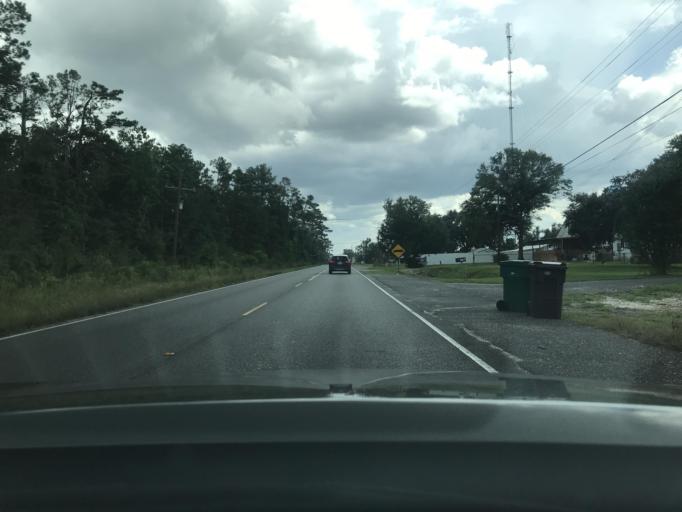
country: US
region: Louisiana
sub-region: Calcasieu Parish
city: Westlake
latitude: 30.2892
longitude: -93.2498
